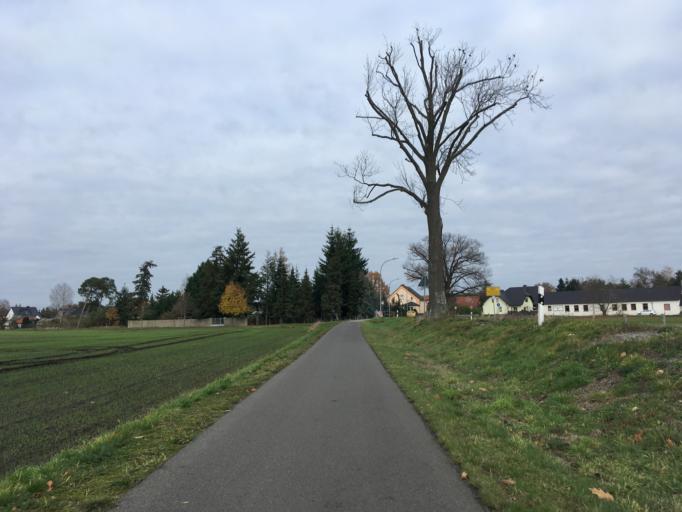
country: DE
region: Brandenburg
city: Peitz
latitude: 51.8807
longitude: 14.4192
